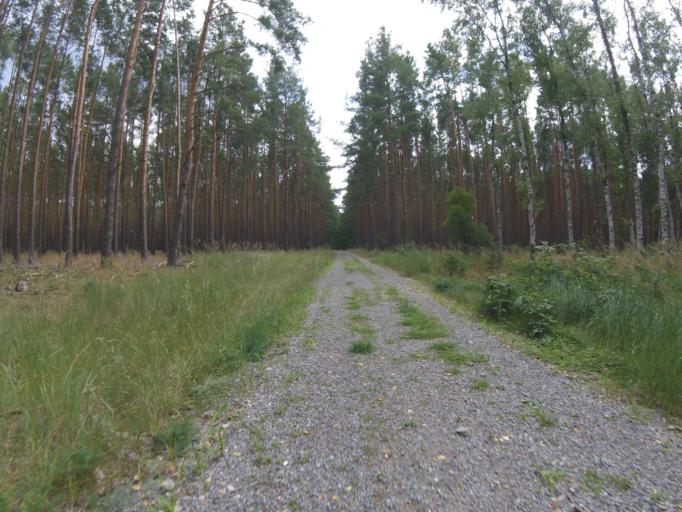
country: DE
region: Brandenburg
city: Gross Koris
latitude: 52.1538
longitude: 13.6728
